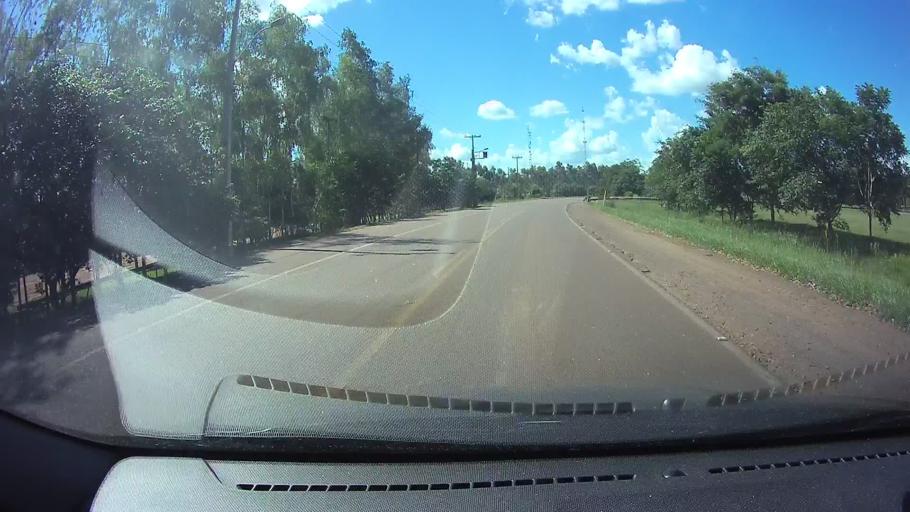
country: PY
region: Guaira
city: Coronel Martinez
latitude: -25.7765
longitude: -56.6517
